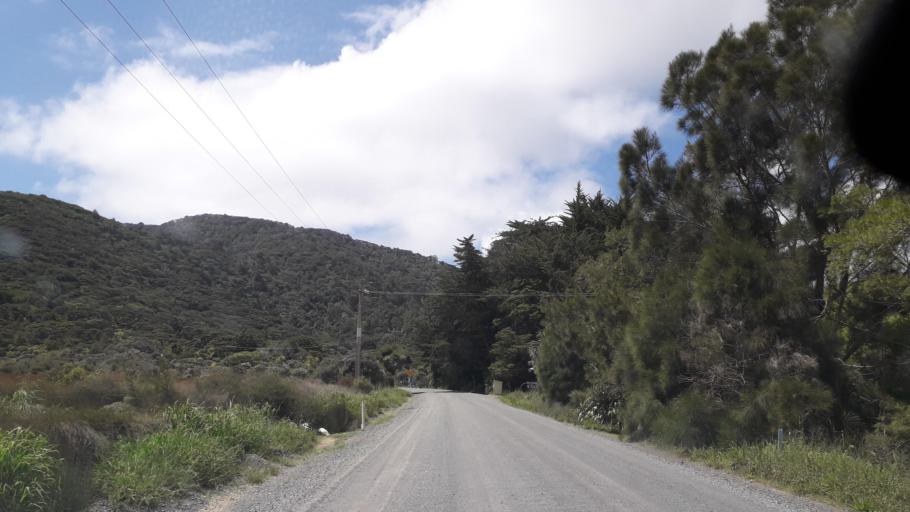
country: NZ
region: Northland
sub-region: Far North District
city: Paihia
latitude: -35.2579
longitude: 174.2667
